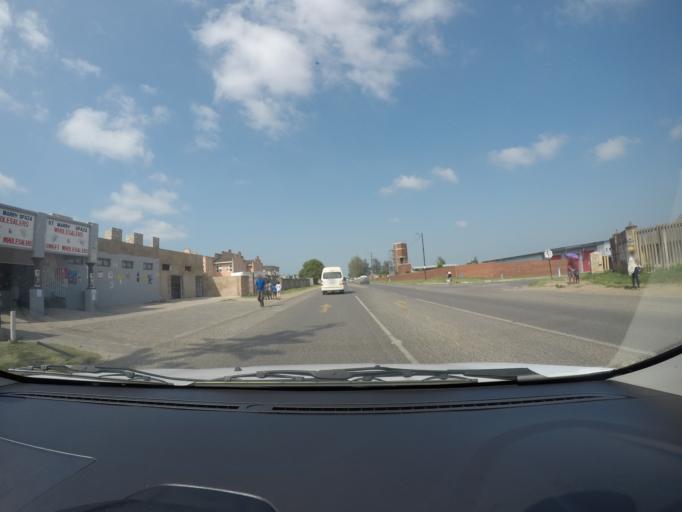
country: ZA
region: KwaZulu-Natal
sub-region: uThungulu District Municipality
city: eSikhawini
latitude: -28.8884
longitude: 31.8959
